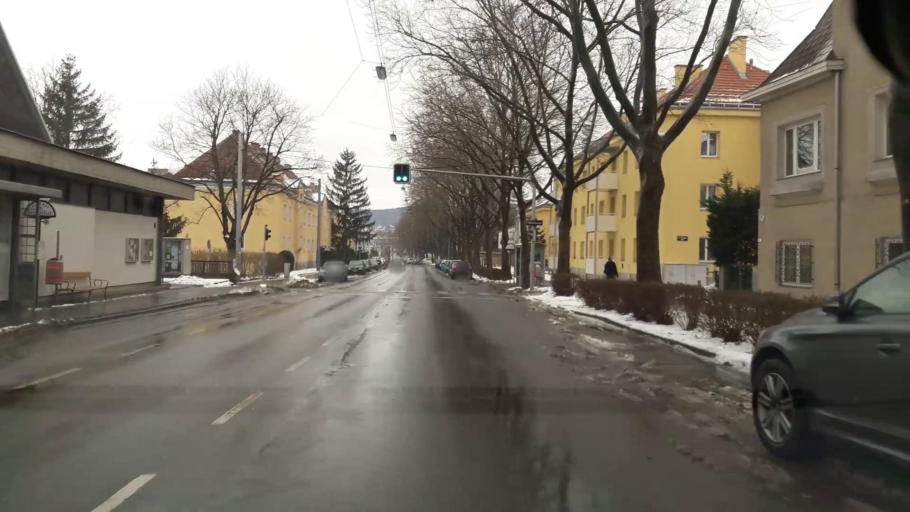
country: AT
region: Lower Austria
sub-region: Politischer Bezirk Modling
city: Perchtoldsdorf
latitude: 48.1725
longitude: 16.2933
